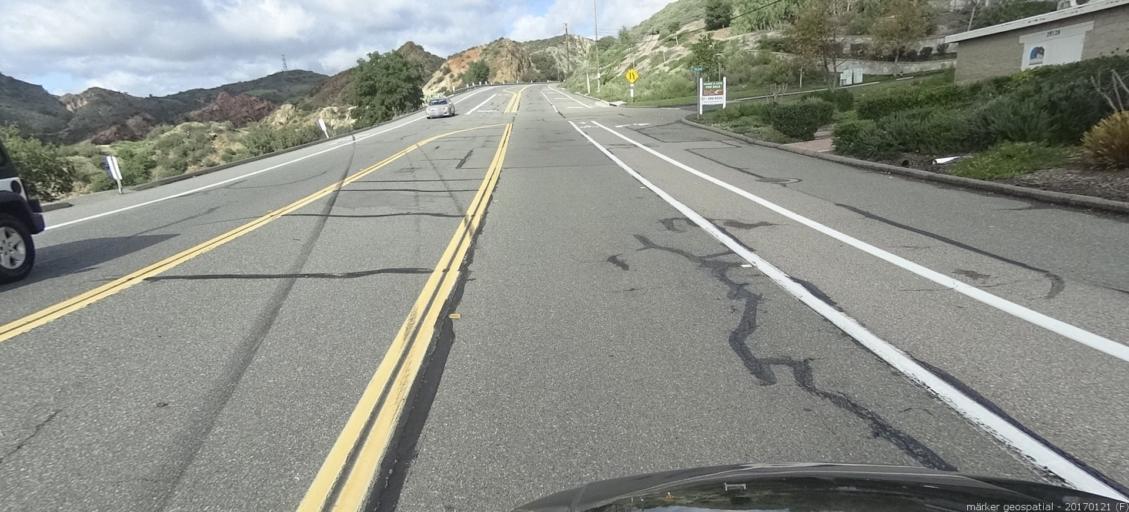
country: US
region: California
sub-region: Orange County
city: Portola Hills
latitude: 33.7007
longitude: -117.6404
